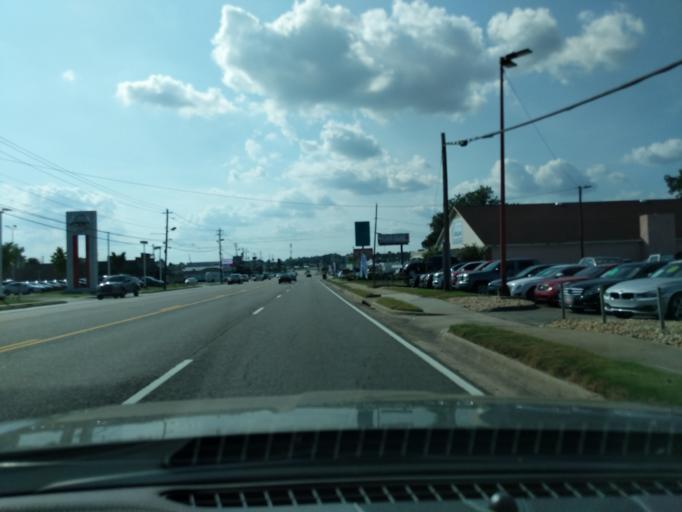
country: US
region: Georgia
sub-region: Columbia County
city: Martinez
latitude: 33.5156
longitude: -82.0671
